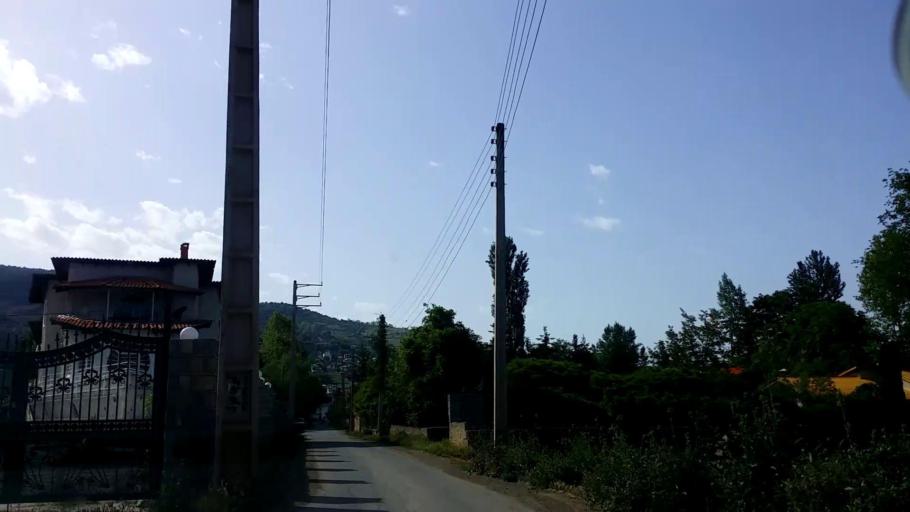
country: IR
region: Mazandaran
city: `Abbasabad
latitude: 36.5212
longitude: 51.1731
